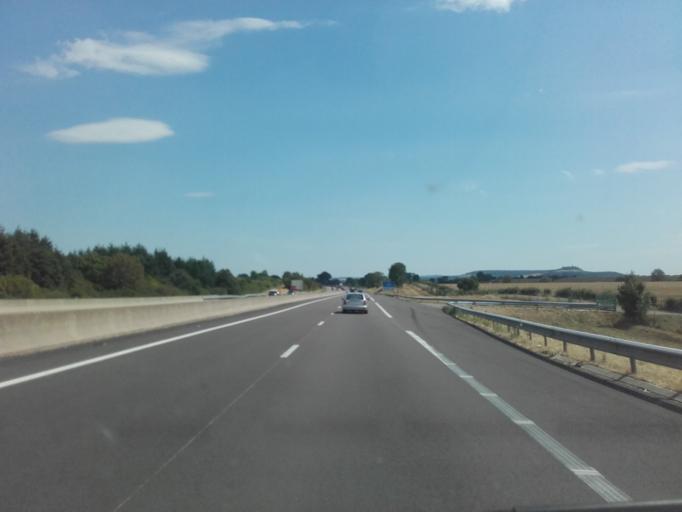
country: FR
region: Bourgogne
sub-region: Departement de la Cote-d'Or
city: Semur-en-Auxois
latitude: 47.4286
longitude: 4.3166
